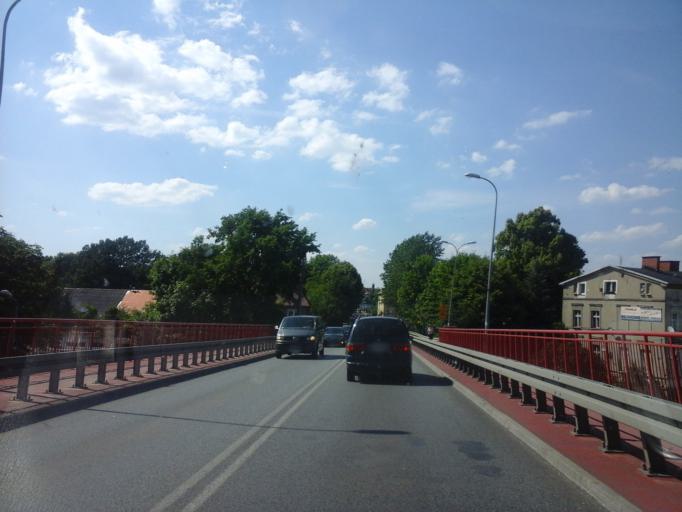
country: PL
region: West Pomeranian Voivodeship
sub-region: Powiat bialogardzki
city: Bialogard
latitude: 54.0069
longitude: 15.9762
